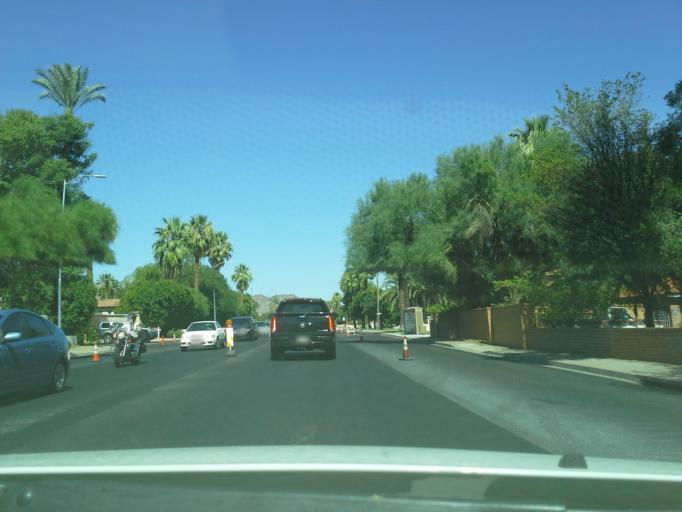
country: US
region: Arizona
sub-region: Maricopa County
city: Phoenix
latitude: 33.5383
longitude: -112.0700
